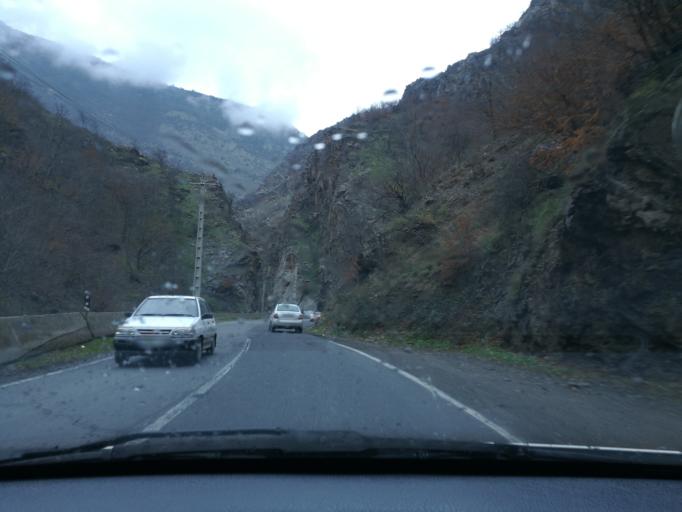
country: IR
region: Mazandaran
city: Chalus
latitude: 36.2855
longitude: 51.2433
